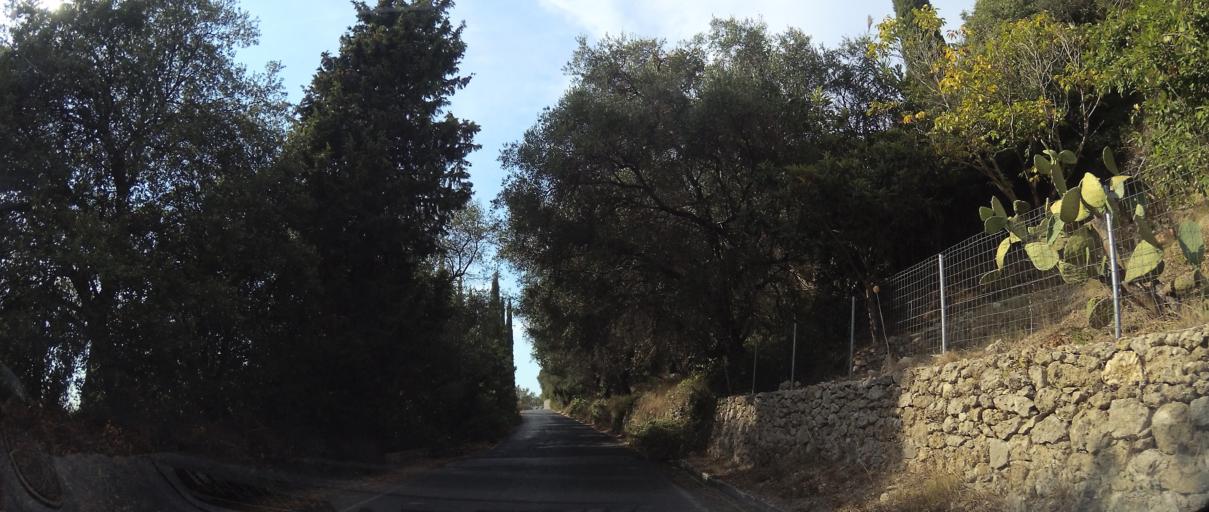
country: GR
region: Ionian Islands
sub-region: Nomos Kerkyras
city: Kynopiastes
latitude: 39.5496
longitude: 19.8652
